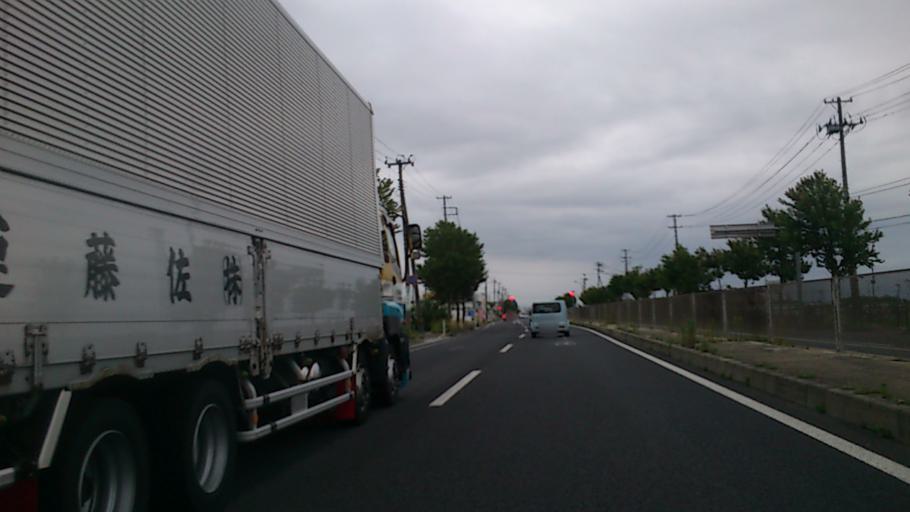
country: JP
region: Yamagata
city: Higashine
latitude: 38.4766
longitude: 140.3829
